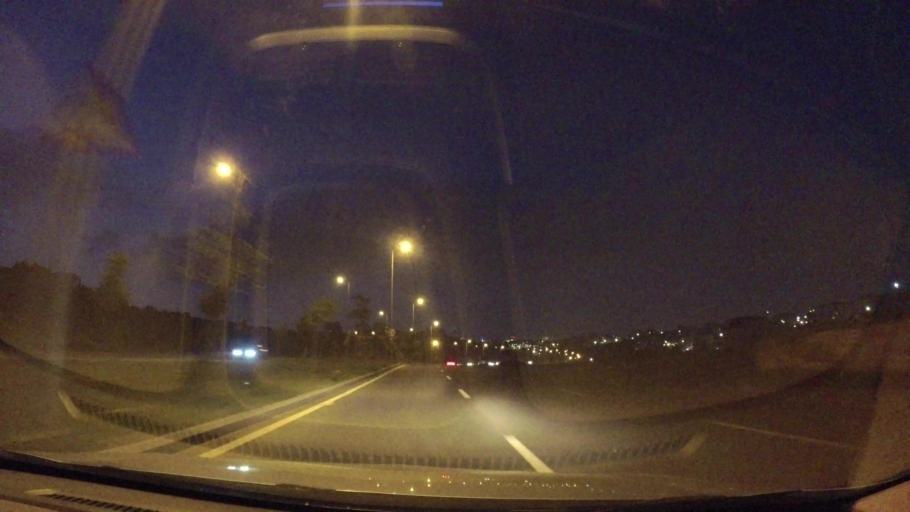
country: JO
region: Amman
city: Al Bunayyat ash Shamaliyah
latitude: 31.9138
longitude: 35.8794
